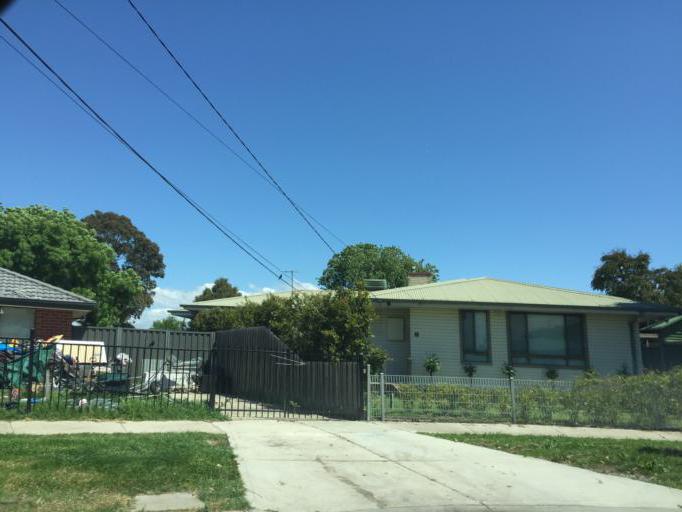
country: AU
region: Victoria
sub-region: Maribyrnong
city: Braybrook
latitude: -37.7837
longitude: 144.8556
